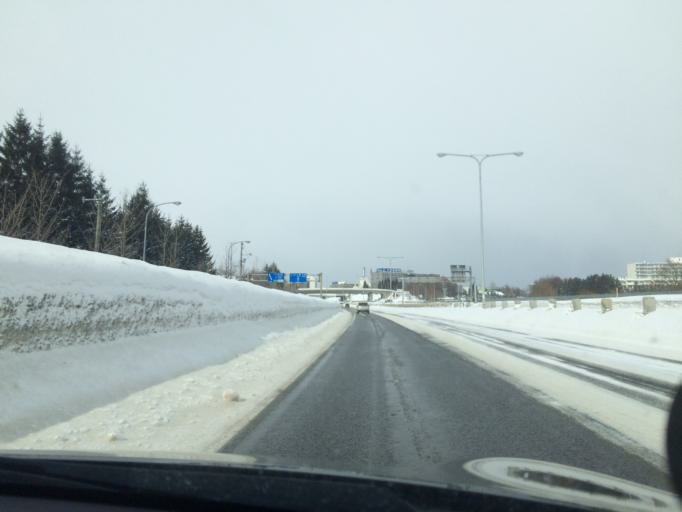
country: JP
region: Hokkaido
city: Kitahiroshima
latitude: 43.0179
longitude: 141.4622
